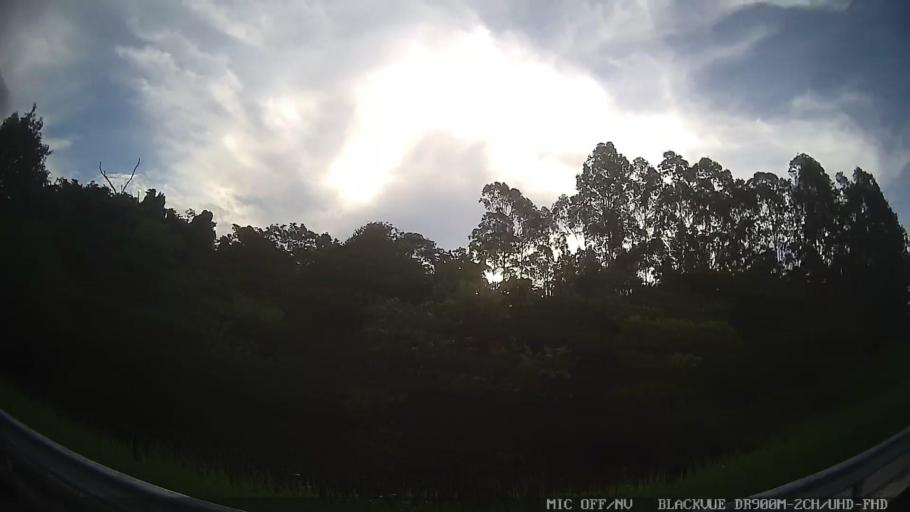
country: BR
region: Sao Paulo
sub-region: Porto Feliz
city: Porto Feliz
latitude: -23.2175
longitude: -47.5710
